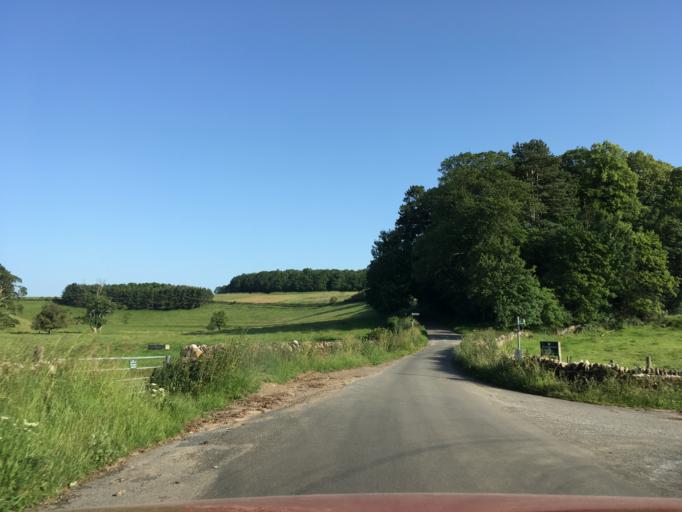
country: GB
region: England
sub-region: Gloucestershire
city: Lechlade
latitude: 51.7610
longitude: -1.7236
